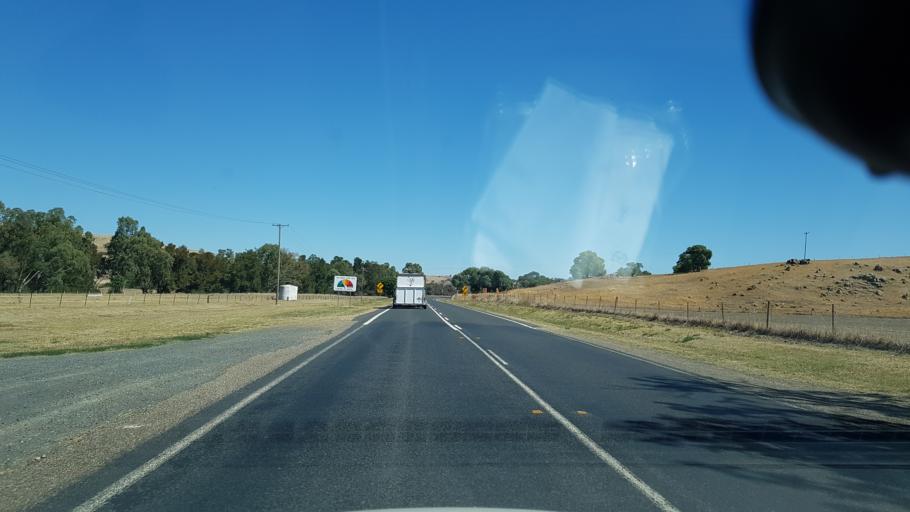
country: AU
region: New South Wales
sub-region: Gundagai
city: Gundagai
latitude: -34.8217
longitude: 148.3500
